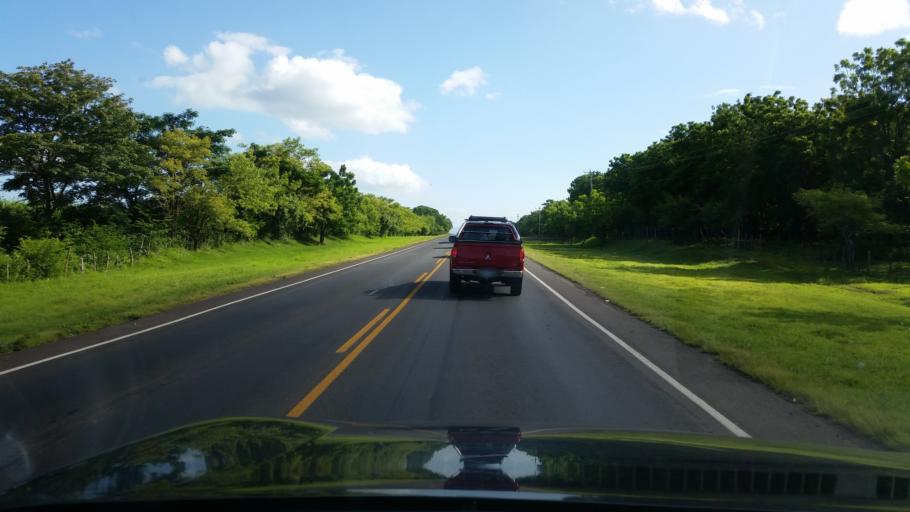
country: NI
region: Managua
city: Tipitapa
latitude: 12.3386
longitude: -86.0511
